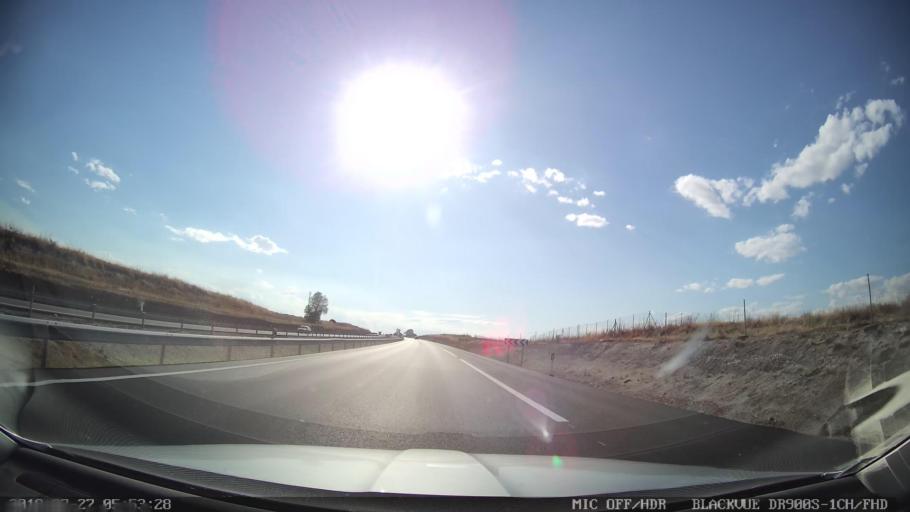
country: ES
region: Castille-La Mancha
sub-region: Province of Toledo
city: Torralba de Oropesa
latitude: 39.9312
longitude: -5.1443
